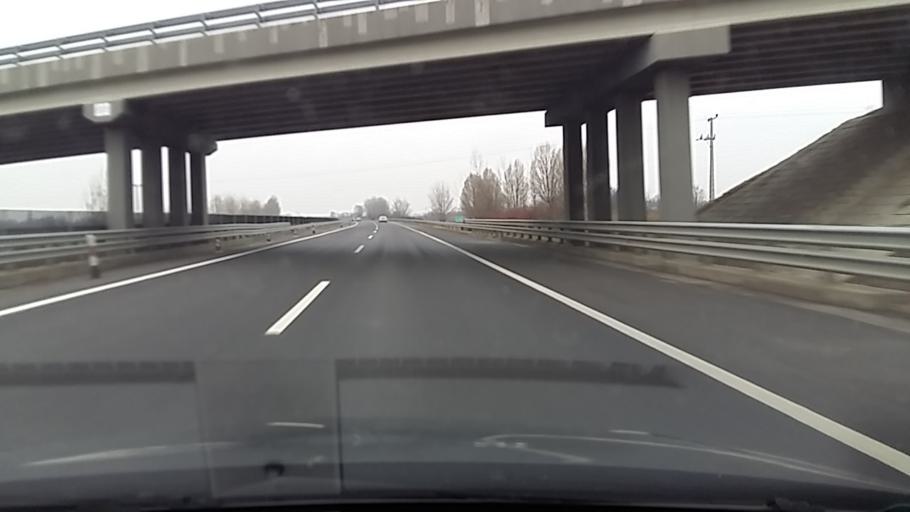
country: HU
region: Szabolcs-Szatmar-Bereg
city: Nyiregyhaza
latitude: 47.8961
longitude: 21.6824
